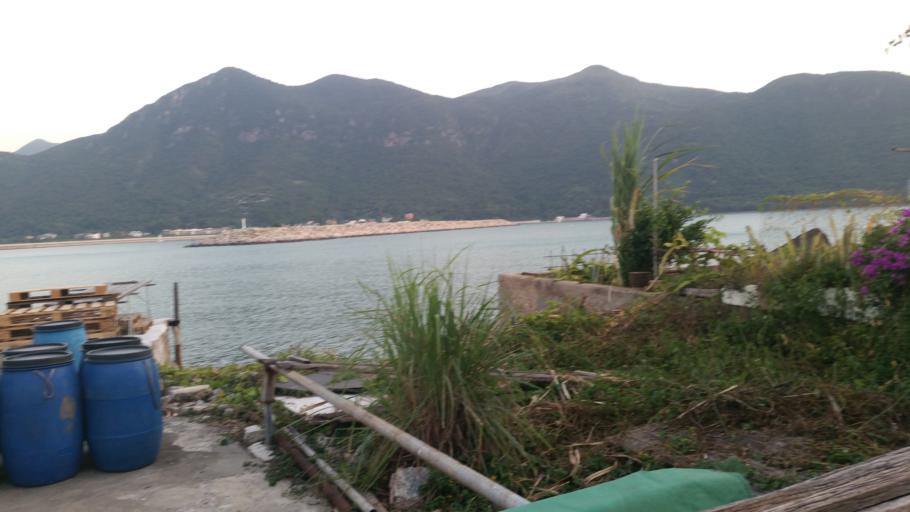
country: HK
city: Tai O
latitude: 22.2538
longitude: 113.8559
